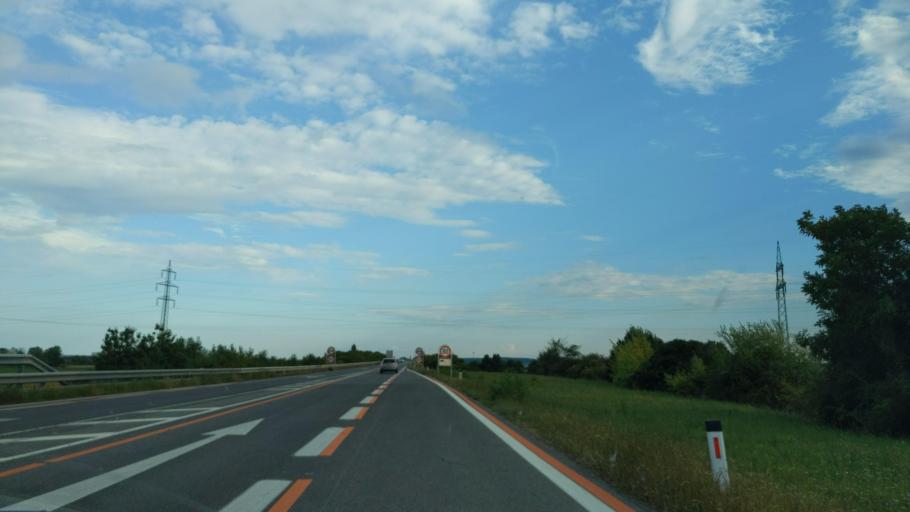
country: AT
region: Burgenland
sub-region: Eisenstadt-Umgebung
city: Wulkaprodersdorf
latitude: 47.8108
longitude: 16.4997
